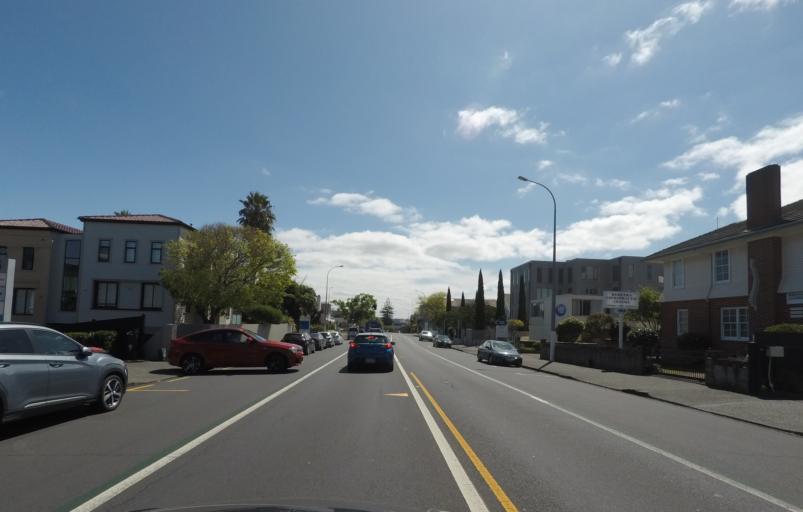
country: NZ
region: Auckland
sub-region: Auckland
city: Auckland
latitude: -36.8736
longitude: 174.7824
